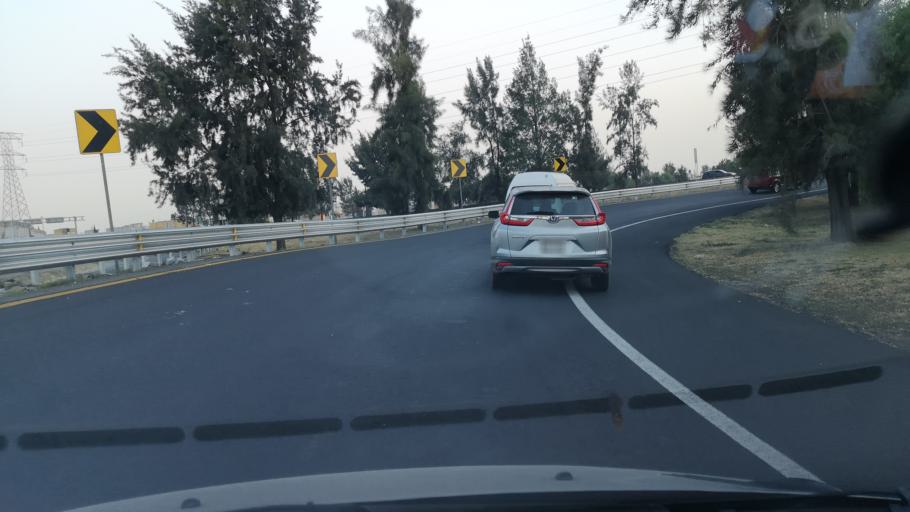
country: MX
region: Mexico
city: Santo Tomas Chiconautla
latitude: 19.6159
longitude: -99.0301
